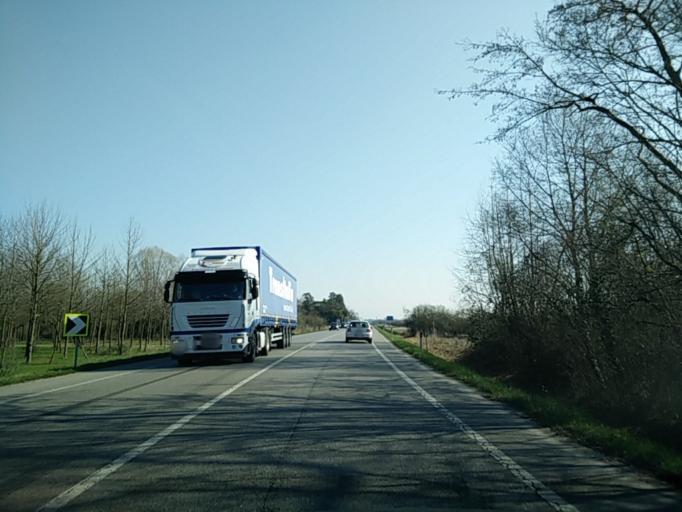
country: IT
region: Friuli Venezia Giulia
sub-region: Provincia di Pordenone
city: Sesto al Reghena
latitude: 45.8891
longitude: 12.8062
